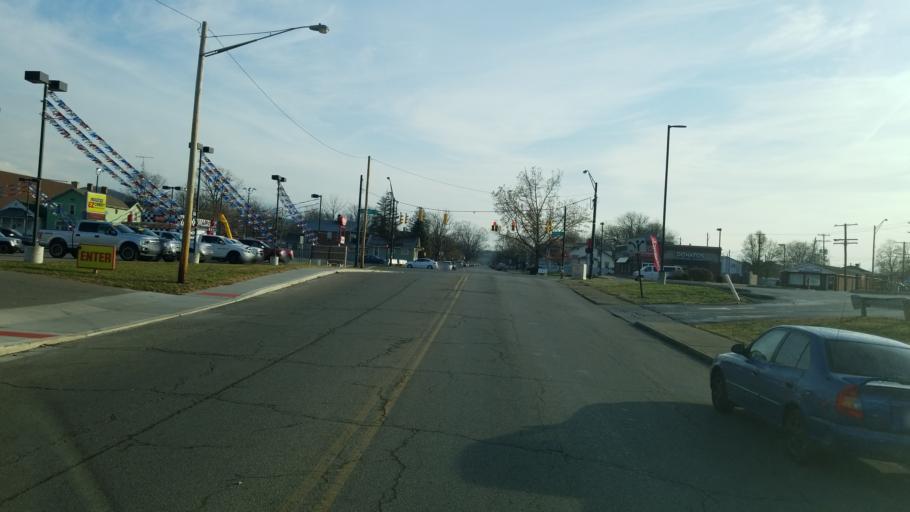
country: US
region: Ohio
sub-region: Ross County
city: Chillicothe
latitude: 39.3369
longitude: -82.9759
